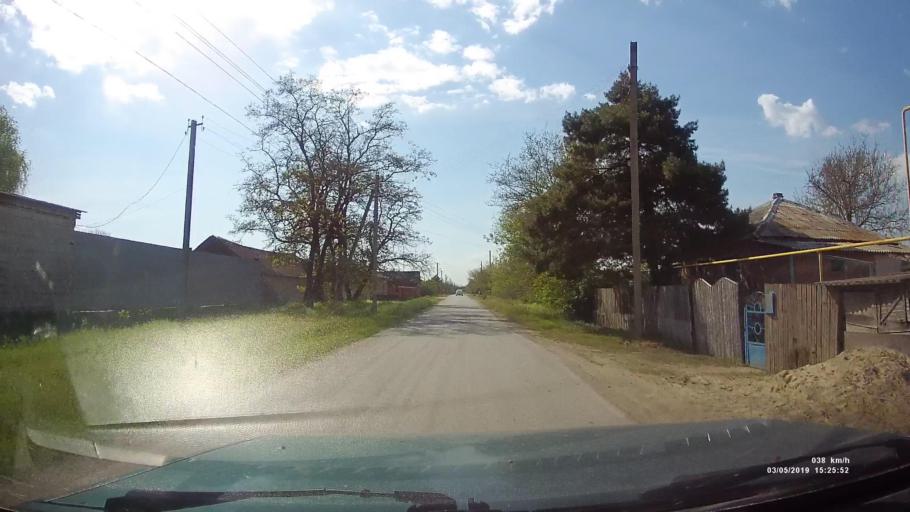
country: RU
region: Rostov
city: Ust'-Donetskiy
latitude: 47.5792
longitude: 40.8557
